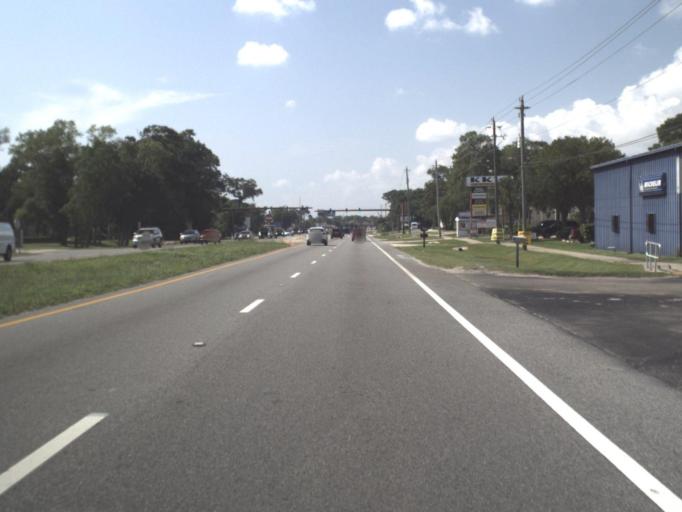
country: US
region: Florida
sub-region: Saint Johns County
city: Saint Augustine
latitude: 29.8775
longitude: -81.3245
